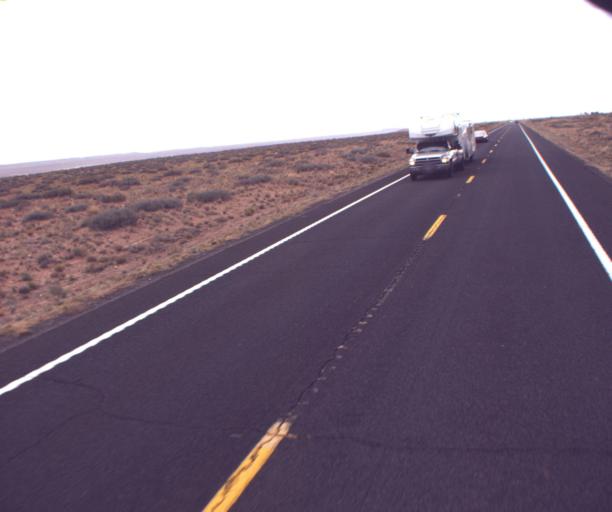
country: US
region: Arizona
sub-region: Coconino County
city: Tuba City
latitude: 36.1589
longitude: -111.1110
